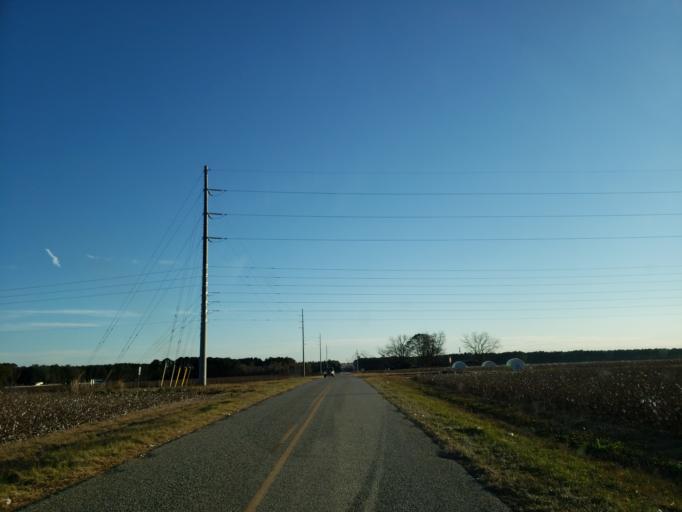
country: US
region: Georgia
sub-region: Dooly County
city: Vienna
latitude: 32.1450
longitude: -83.7610
